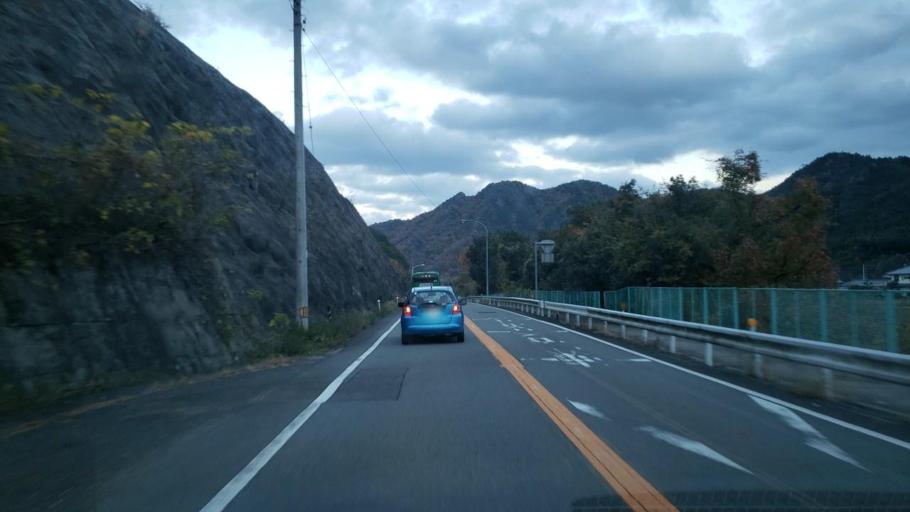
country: JP
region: Tokushima
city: Kamojimacho-jogejima
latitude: 34.2179
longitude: 134.3345
